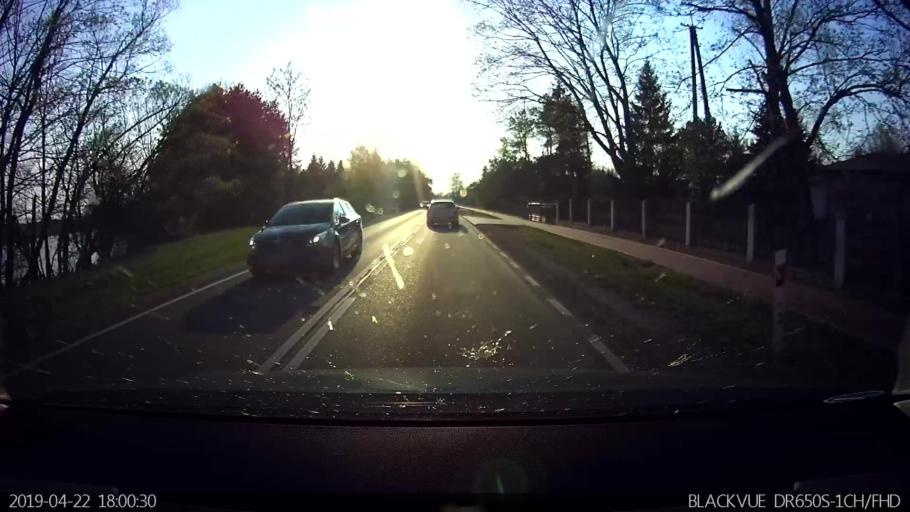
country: PL
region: Masovian Voivodeship
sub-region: Powiat wegrowski
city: Korytnica
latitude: 52.4763
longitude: 21.8455
